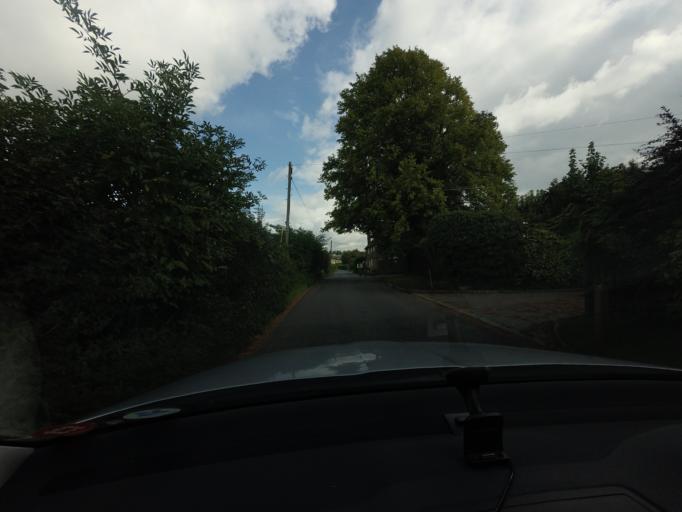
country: GB
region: England
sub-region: Kent
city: Borough Green
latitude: 51.3097
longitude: 0.2940
